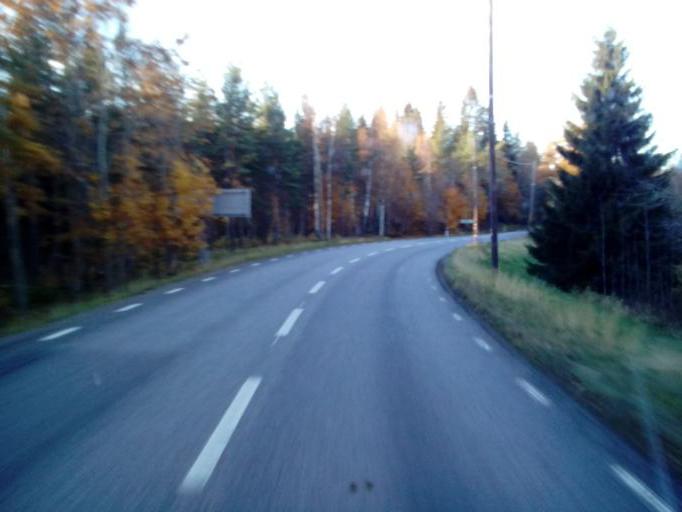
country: SE
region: OErebro
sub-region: Hallsbergs Kommun
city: Palsboda
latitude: 59.0755
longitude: 15.3305
